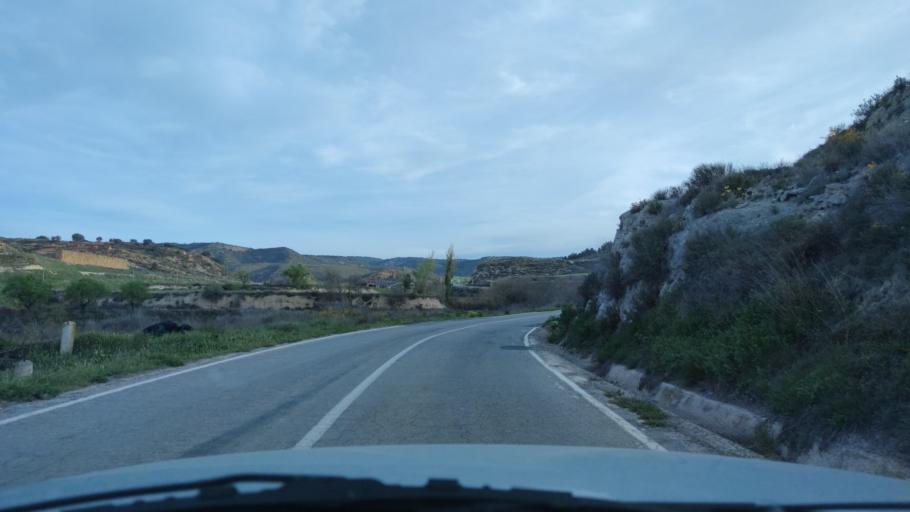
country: ES
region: Catalonia
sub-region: Provincia de Lleida
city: Balaguer
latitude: 41.8286
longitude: 0.7994
